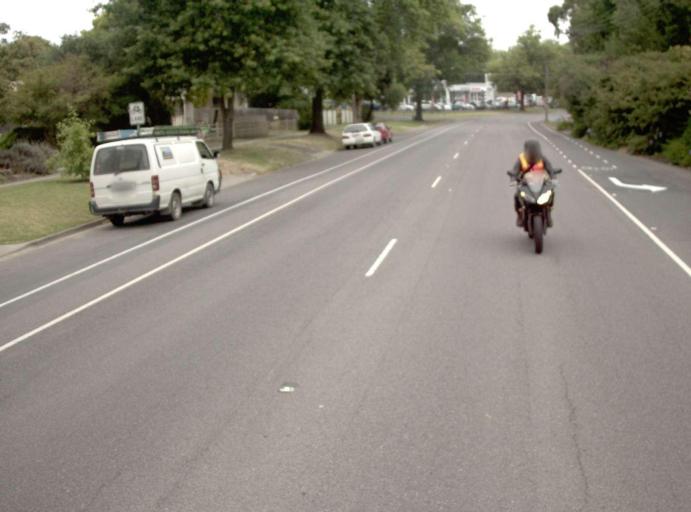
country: AU
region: Victoria
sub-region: Yarra Ranges
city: Healesville
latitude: -37.6559
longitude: 145.5117
